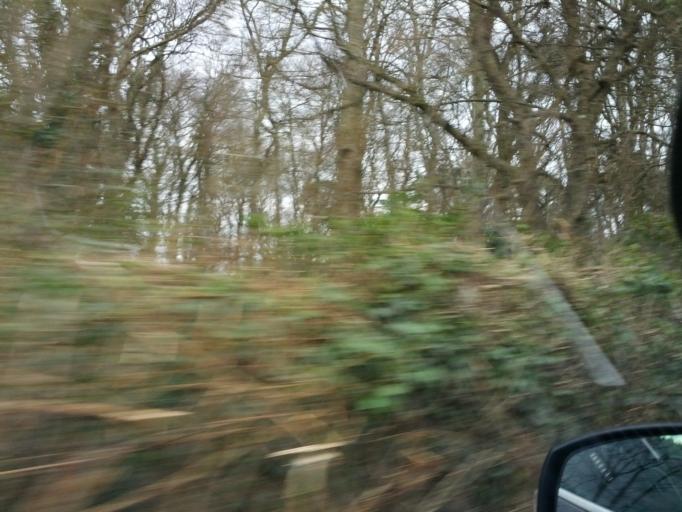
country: IE
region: Connaught
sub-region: County Galway
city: Oranmore
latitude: 53.1794
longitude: -8.9016
